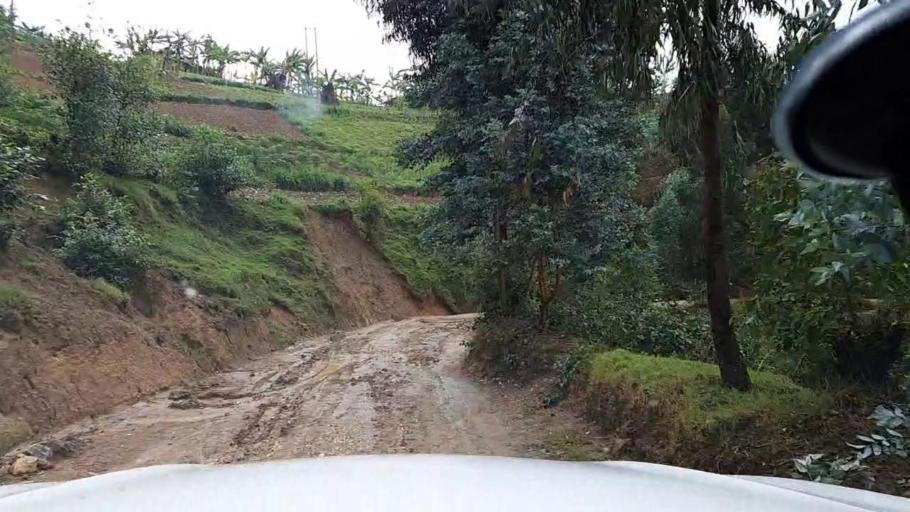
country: RW
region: Western Province
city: Kibuye
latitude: -2.0829
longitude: 29.5119
